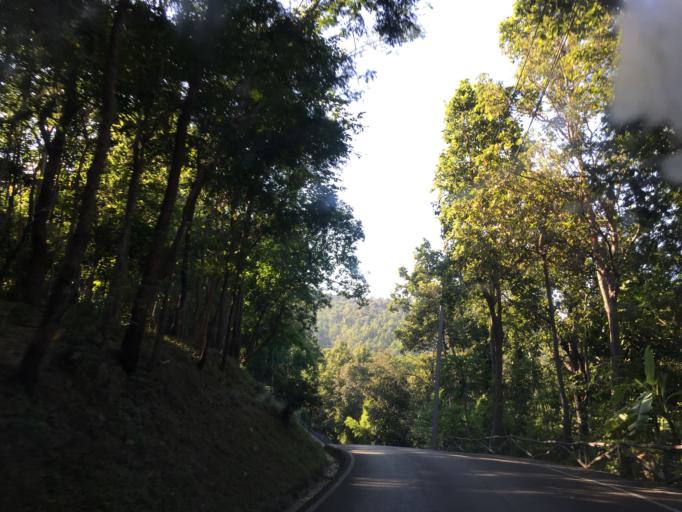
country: TH
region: Chiang Mai
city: Chiang Mai
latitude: 18.8028
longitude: 98.9438
